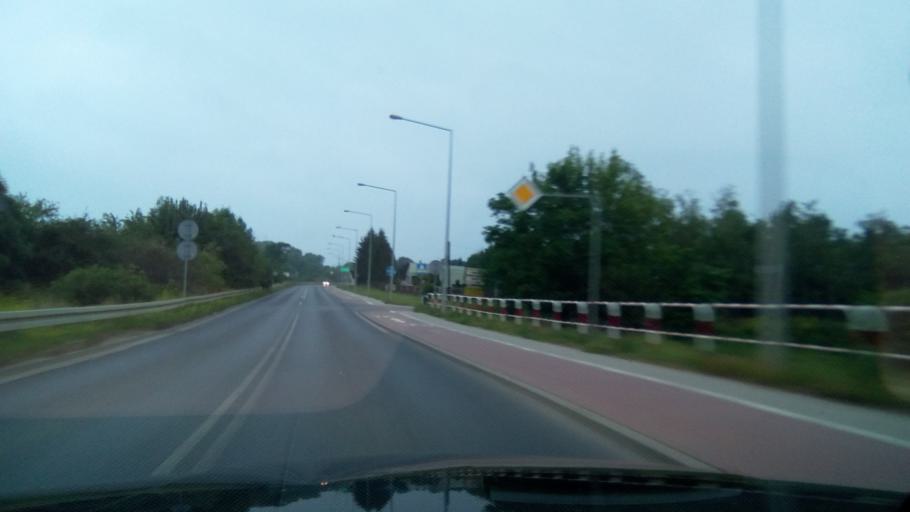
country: PL
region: Greater Poland Voivodeship
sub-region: Powiat poznanski
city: Swarzedz
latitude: 52.4263
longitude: 17.0795
